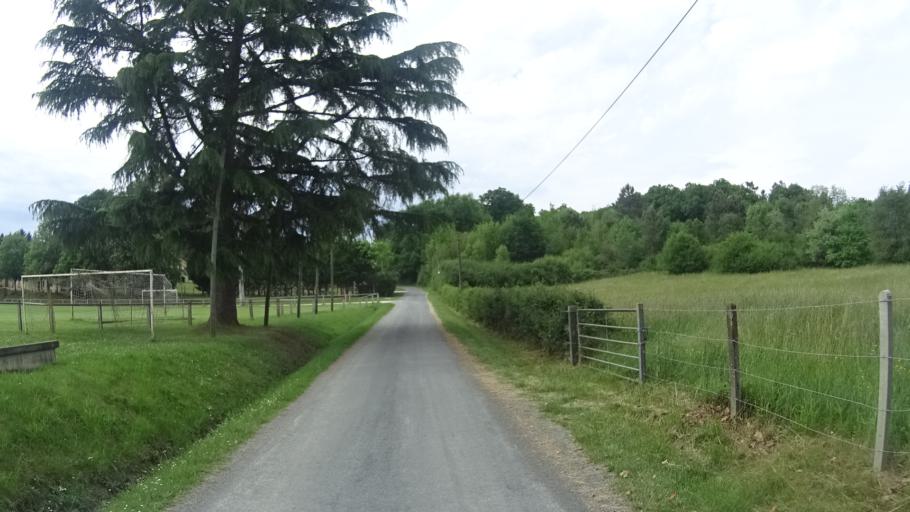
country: FR
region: Aquitaine
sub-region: Departement de la Dordogne
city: Neuvic
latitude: 45.0240
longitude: 0.5377
